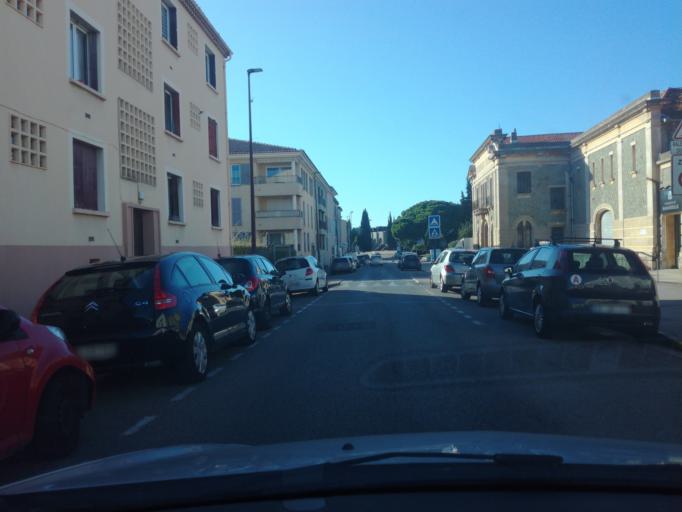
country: FR
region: Provence-Alpes-Cote d'Azur
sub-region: Departement du Var
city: Frejus
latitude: 43.4333
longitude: 6.7313
